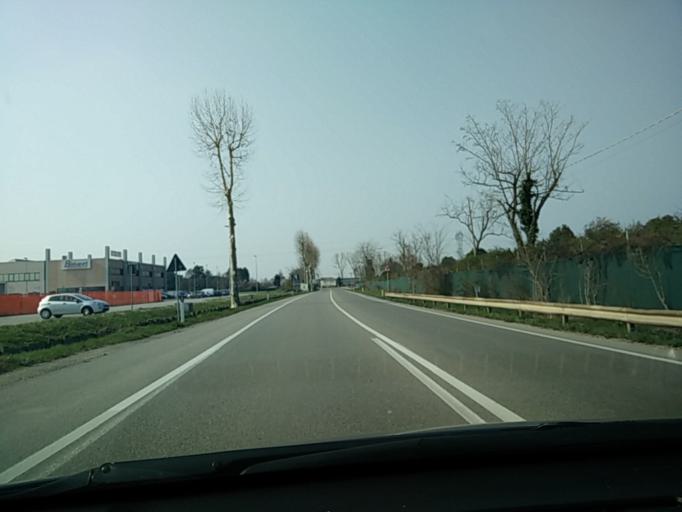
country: IT
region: Veneto
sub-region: Provincia di Treviso
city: Castagnole
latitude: 45.7051
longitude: 12.1740
